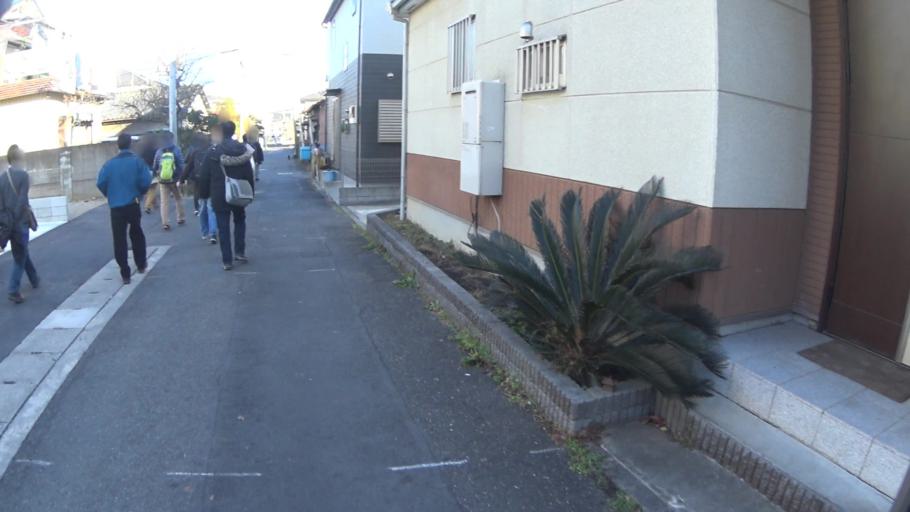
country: JP
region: Saitama
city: Shimotoda
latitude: 35.8454
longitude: 139.6899
